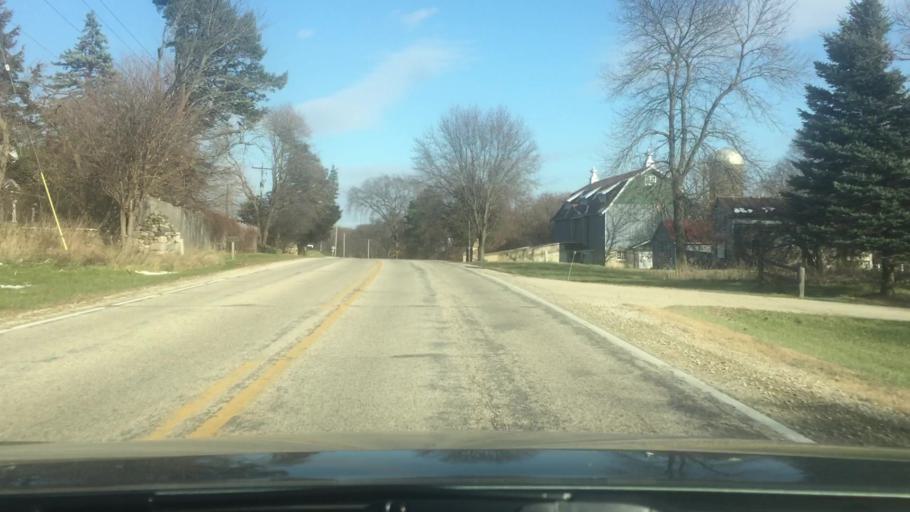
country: US
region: Wisconsin
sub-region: Jefferson County
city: Palmyra
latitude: 42.9386
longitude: -88.6113
